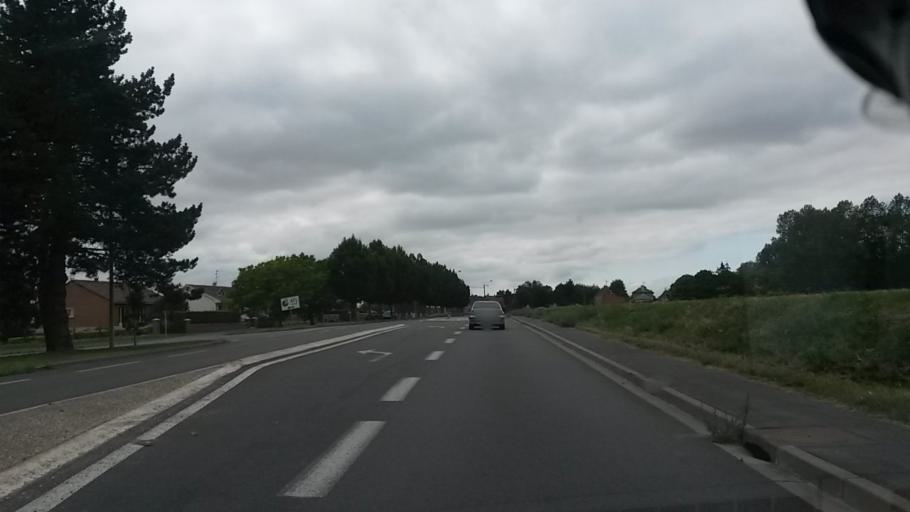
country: FR
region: Nord-Pas-de-Calais
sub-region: Departement du Nord
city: Raillencourt-Sainte-Olle
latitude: 50.1700
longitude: 3.1736
